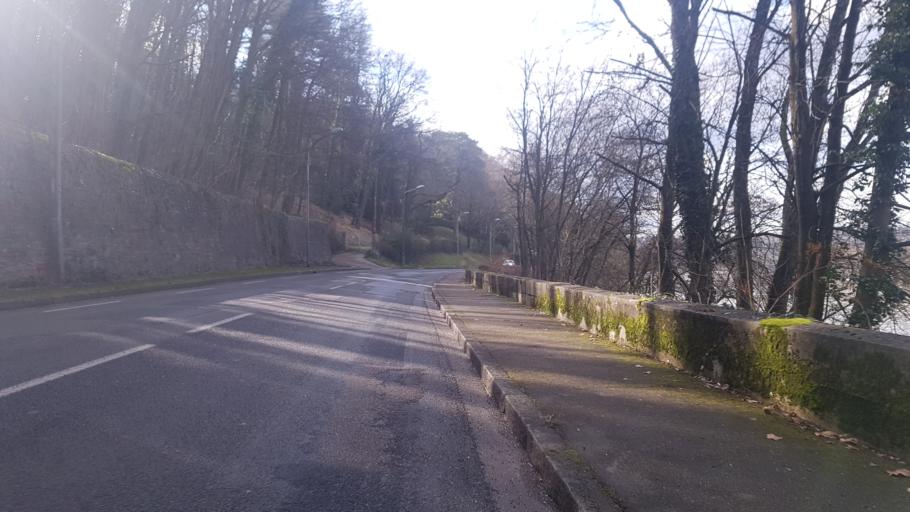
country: FR
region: Rhone-Alpes
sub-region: Departement du Rhone
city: Sathonay-Camp
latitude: 45.8172
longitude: 4.8561
